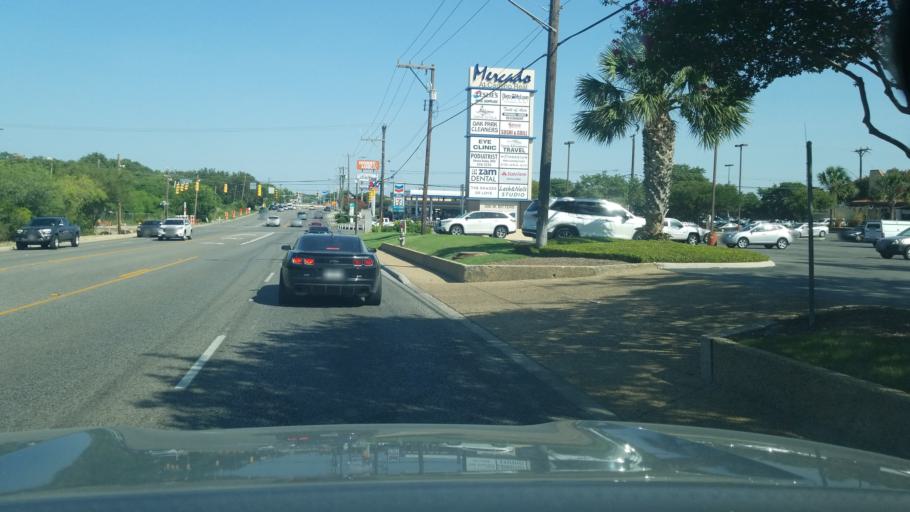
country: US
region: Texas
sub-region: Bexar County
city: Hollywood Park
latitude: 29.5688
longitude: -98.4876
